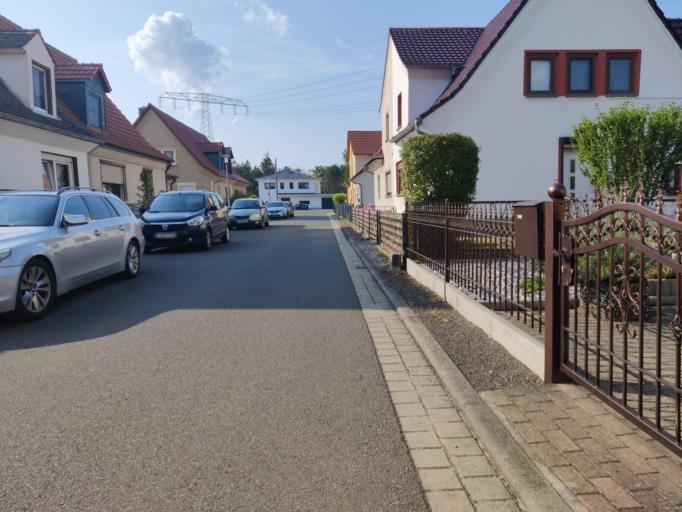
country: DE
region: Saxony
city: Neukieritzsch
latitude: 51.1529
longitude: 12.4154
